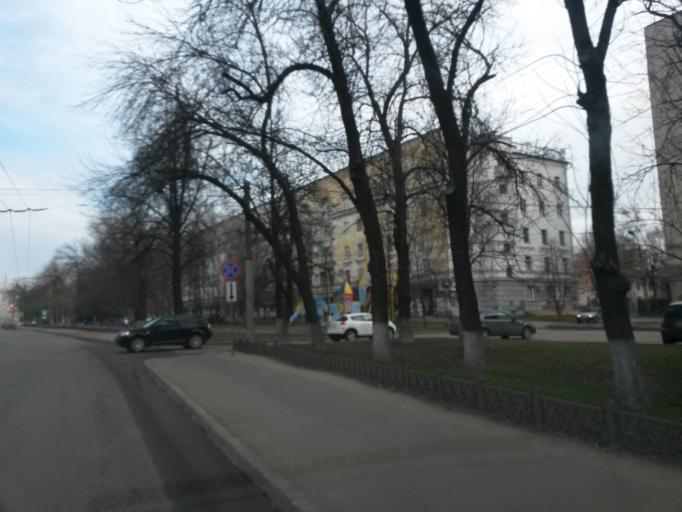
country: RU
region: Jaroslavl
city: Yaroslavl
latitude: 57.6387
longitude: 39.8777
